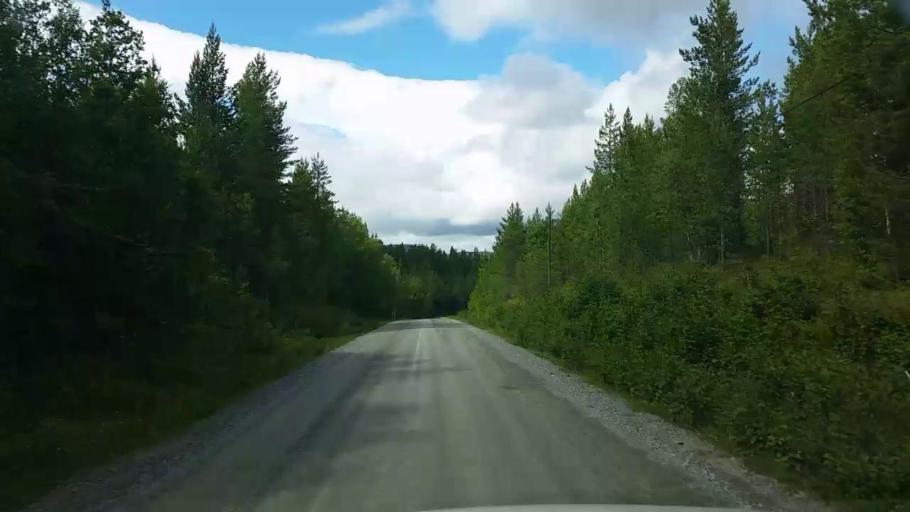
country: NO
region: Hedmark
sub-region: Engerdal
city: Engerdal
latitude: 62.4190
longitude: 12.6773
